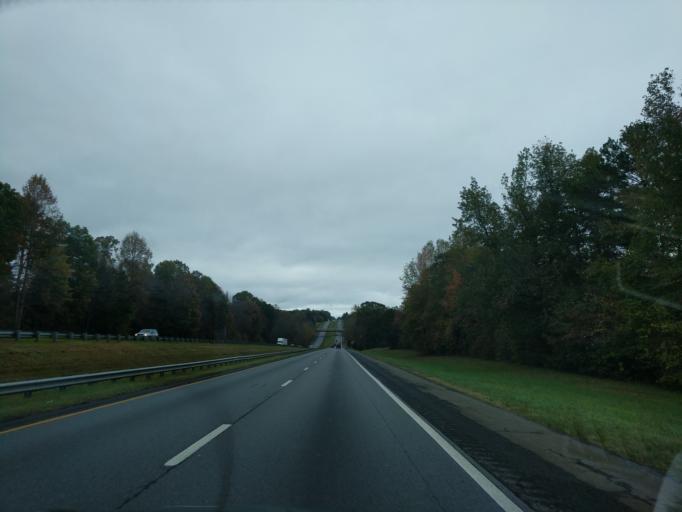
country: US
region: North Carolina
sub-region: Cleveland County
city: Kings Mountain
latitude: 35.2068
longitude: -81.3584
